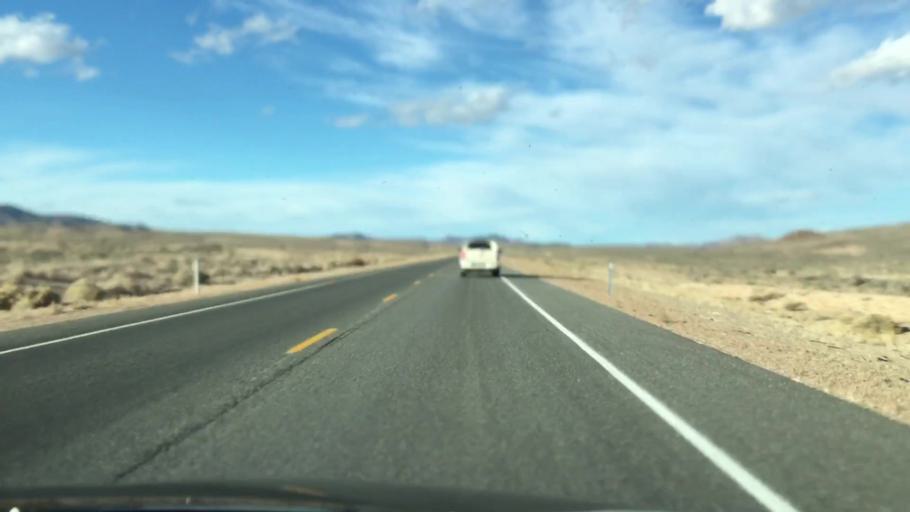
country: US
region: Nevada
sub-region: Esmeralda County
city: Goldfield
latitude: 37.5500
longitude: -117.1969
